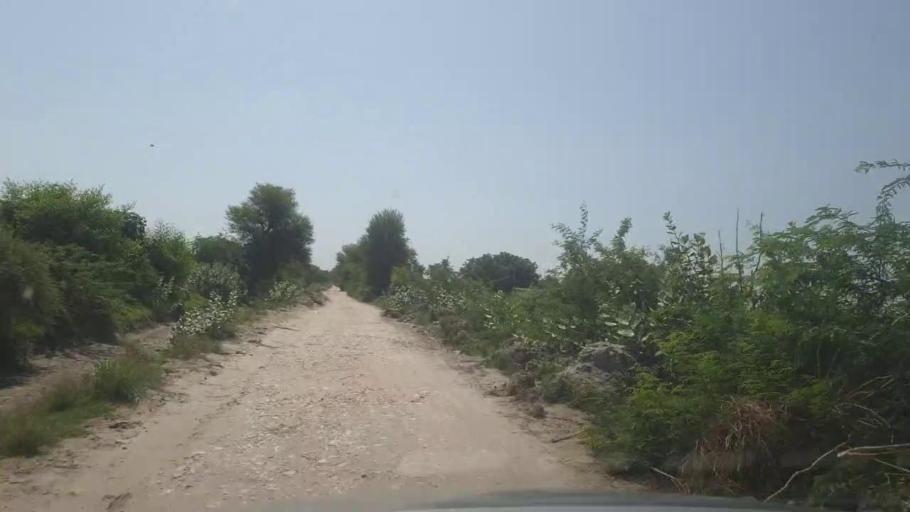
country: PK
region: Sindh
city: Khairpur
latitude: 27.3645
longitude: 69.0251
